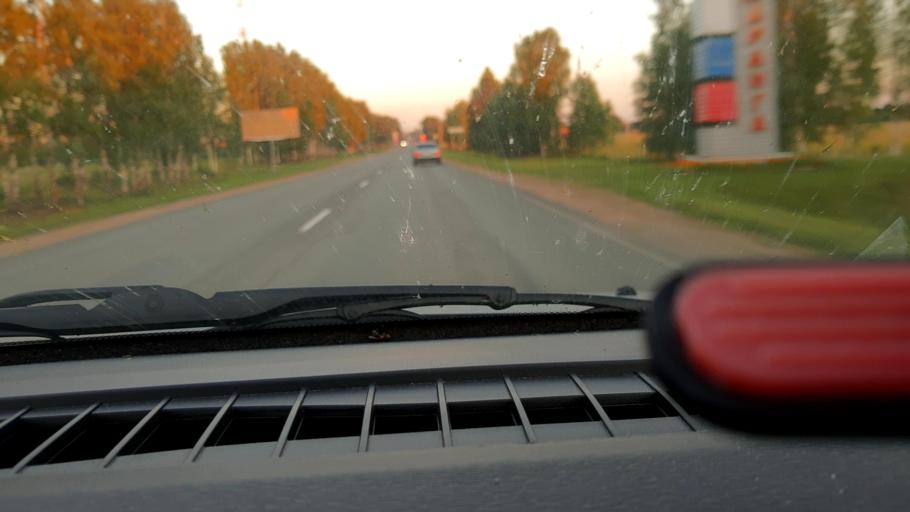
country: RU
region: Nizjnij Novgorod
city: Sharanga
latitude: 57.1979
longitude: 46.5255
